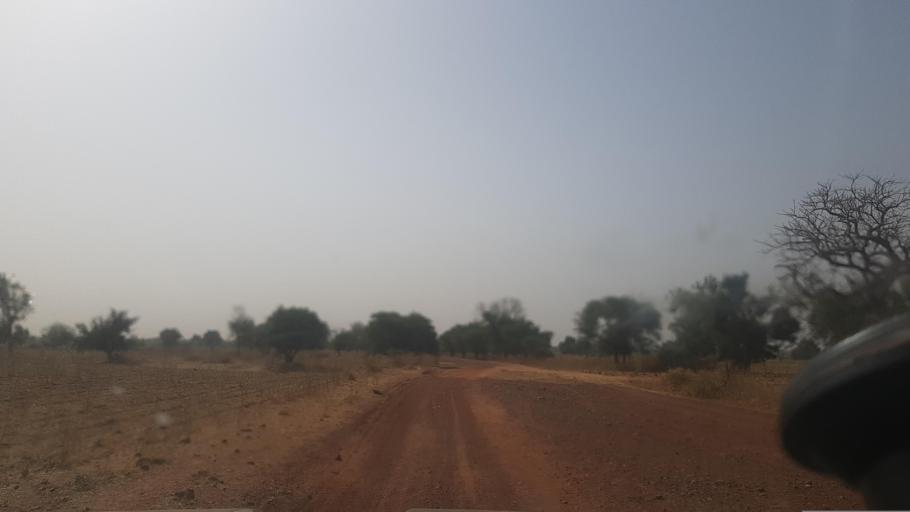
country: ML
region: Segou
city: Baroueli
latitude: 13.1475
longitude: -6.5159
